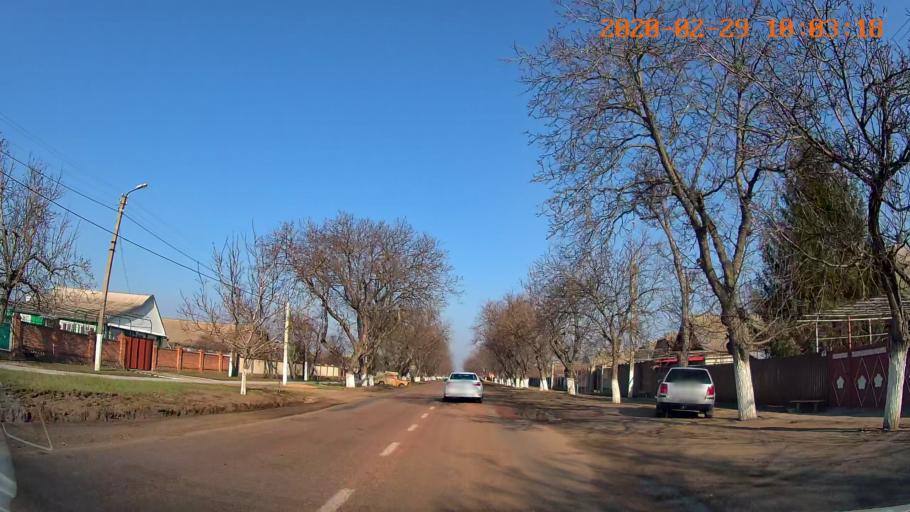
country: MD
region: Causeni
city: Chitcani
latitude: 46.7895
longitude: 29.6808
